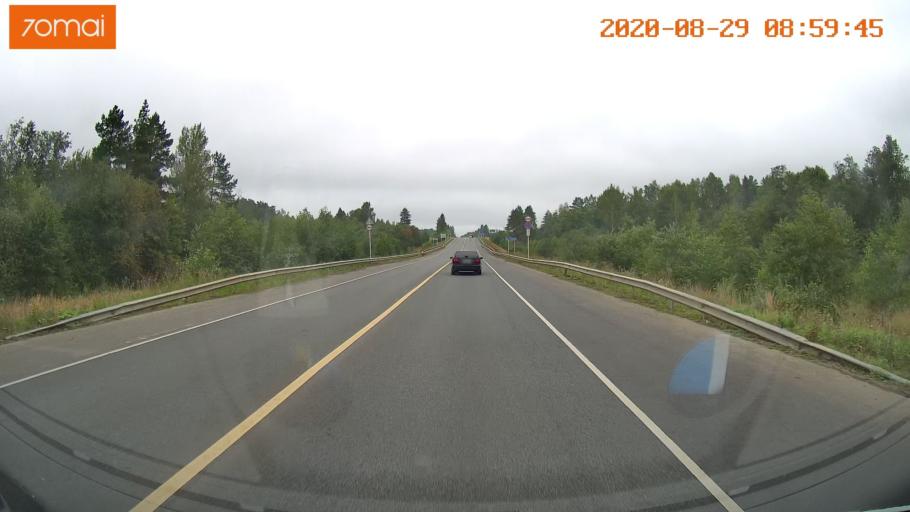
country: RU
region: Ivanovo
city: Staraya Vichuga
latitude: 57.2955
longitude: 41.9088
